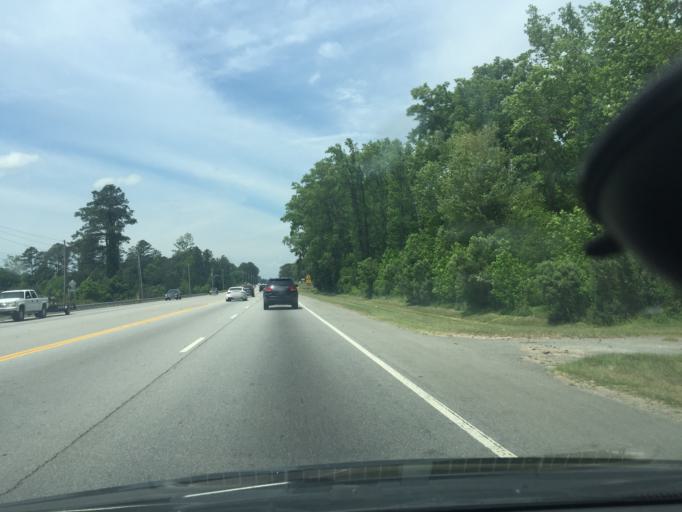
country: US
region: Georgia
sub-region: Chatham County
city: Bloomingdale
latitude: 32.1377
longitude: -81.3151
